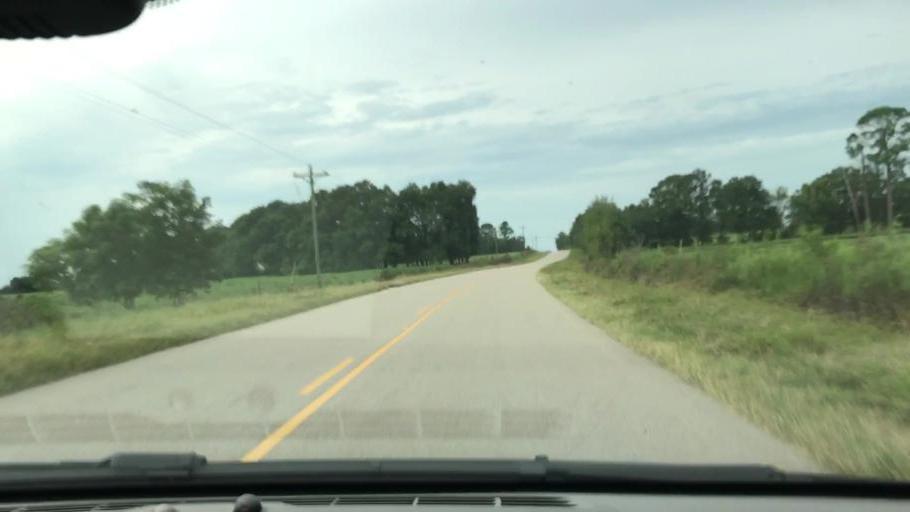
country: US
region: Alabama
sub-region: Houston County
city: Ashford
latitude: 31.2258
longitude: -85.1840
